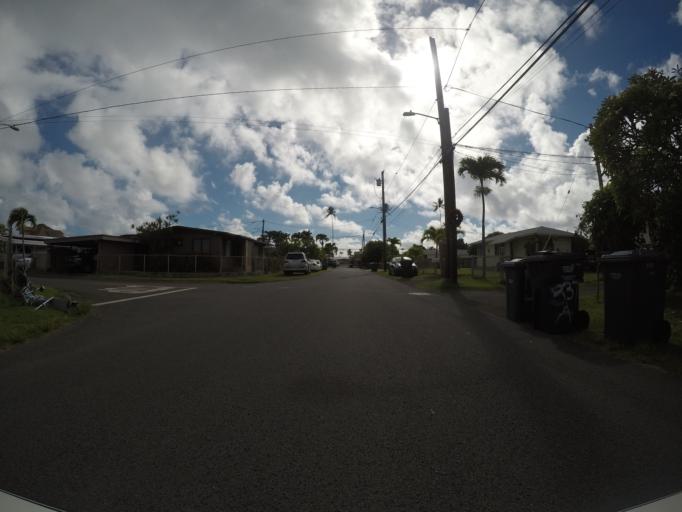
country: US
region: Hawaii
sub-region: Honolulu County
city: Kailua
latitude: 21.4013
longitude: -157.7451
